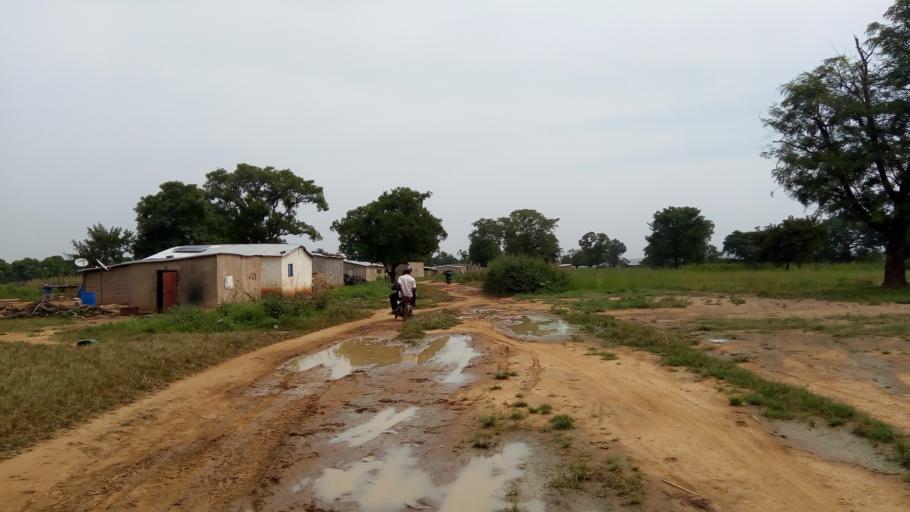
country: ML
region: Koulikoro
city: Kangaba
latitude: 11.6779
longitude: -8.6756
